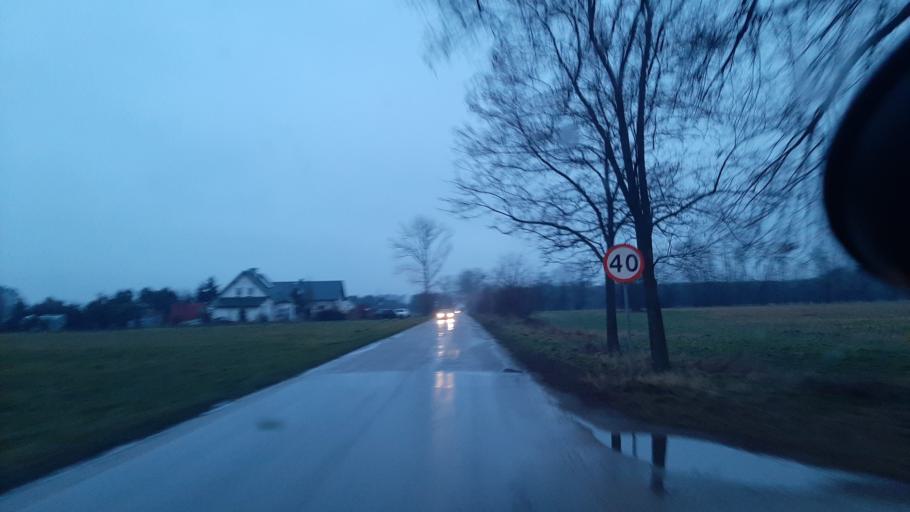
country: PL
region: Lublin Voivodeship
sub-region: Powiat lubartowski
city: Kamionka
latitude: 51.3996
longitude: 22.4117
